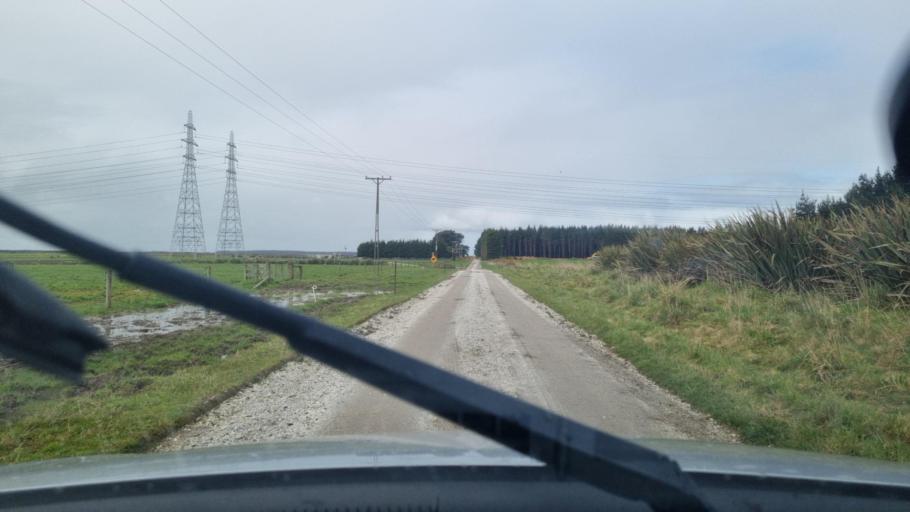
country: NZ
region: Southland
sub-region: Invercargill City
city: Invercargill
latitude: -46.4919
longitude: 168.4331
